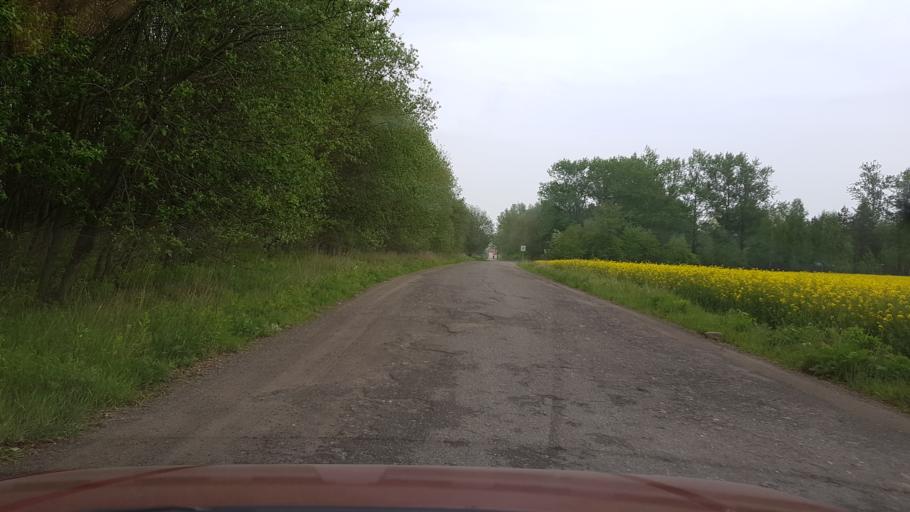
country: PL
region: West Pomeranian Voivodeship
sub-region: Koszalin
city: Koszalin
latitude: 54.1688
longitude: 16.1989
